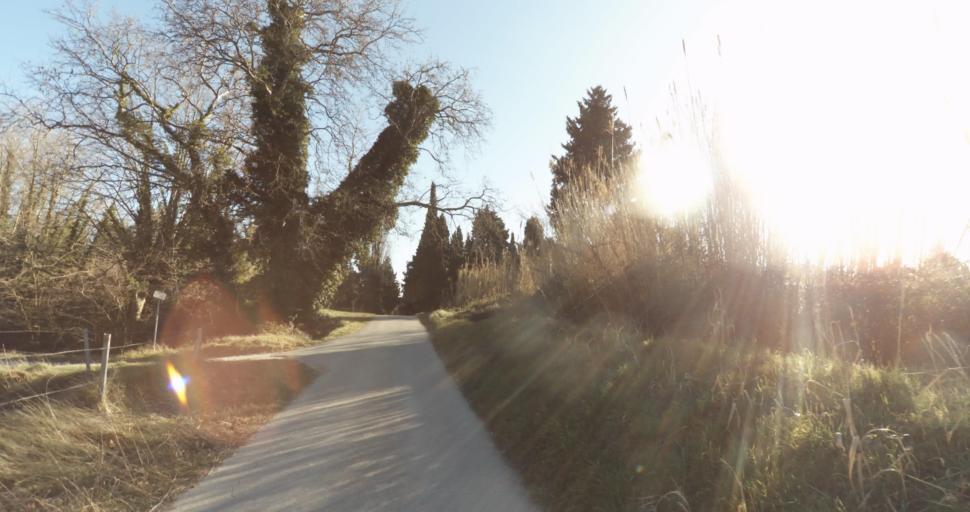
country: FR
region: Provence-Alpes-Cote d'Azur
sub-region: Departement des Bouches-du-Rhone
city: Barbentane
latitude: 43.9138
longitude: 4.7478
